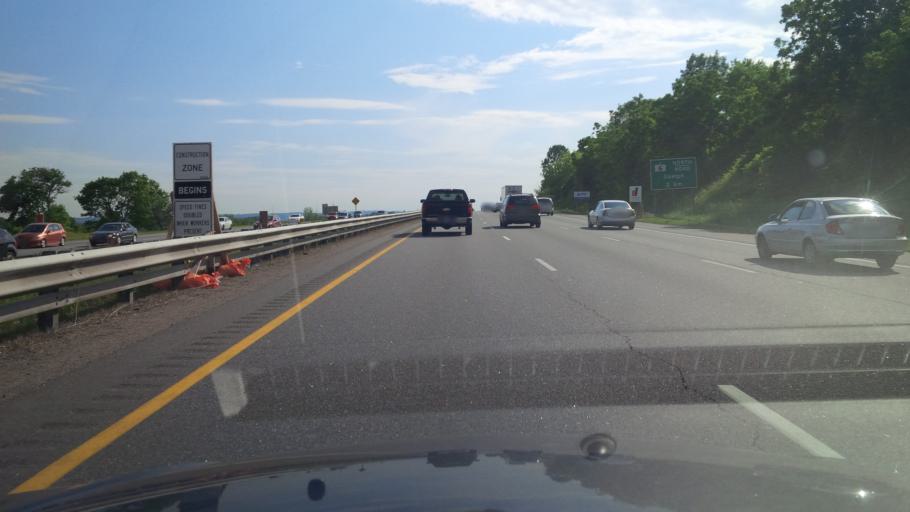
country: CA
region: Ontario
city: Hamilton
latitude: 43.3055
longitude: -79.8689
